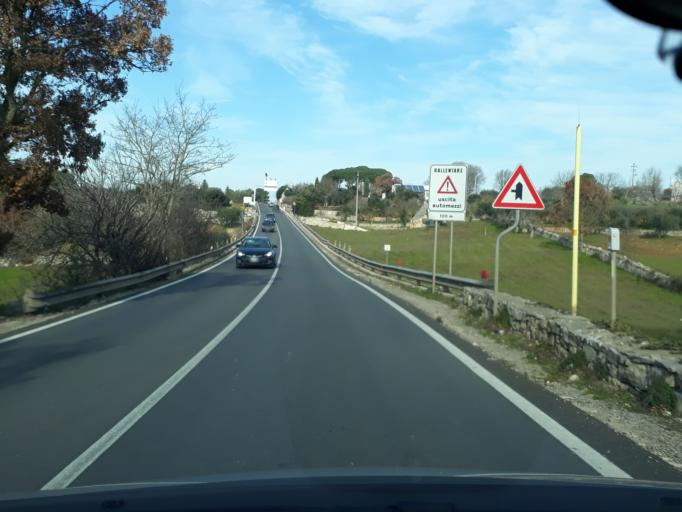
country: IT
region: Apulia
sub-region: Provincia di Bari
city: Locorotondo
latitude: 40.7653
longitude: 17.3326
